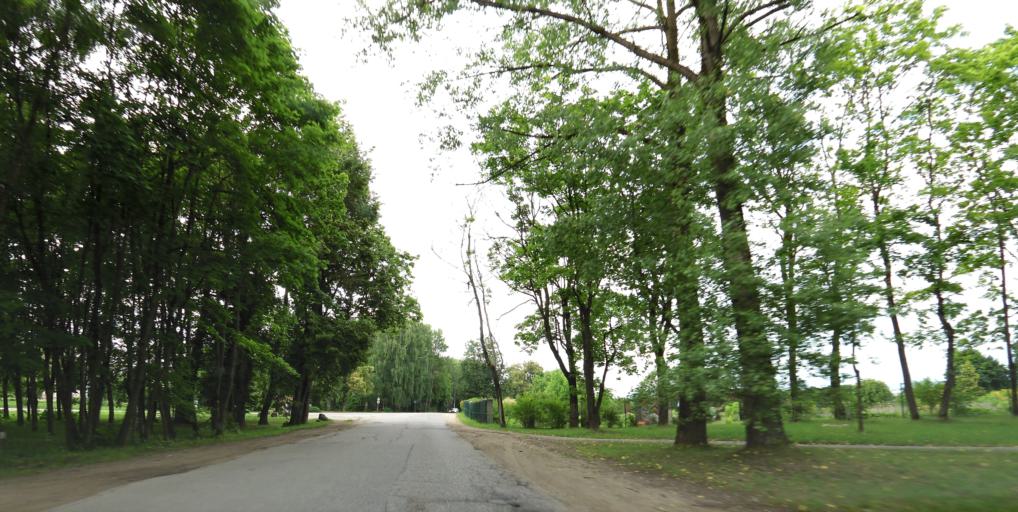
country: LT
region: Vilnius County
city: Pilaite
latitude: 54.7162
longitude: 25.1964
